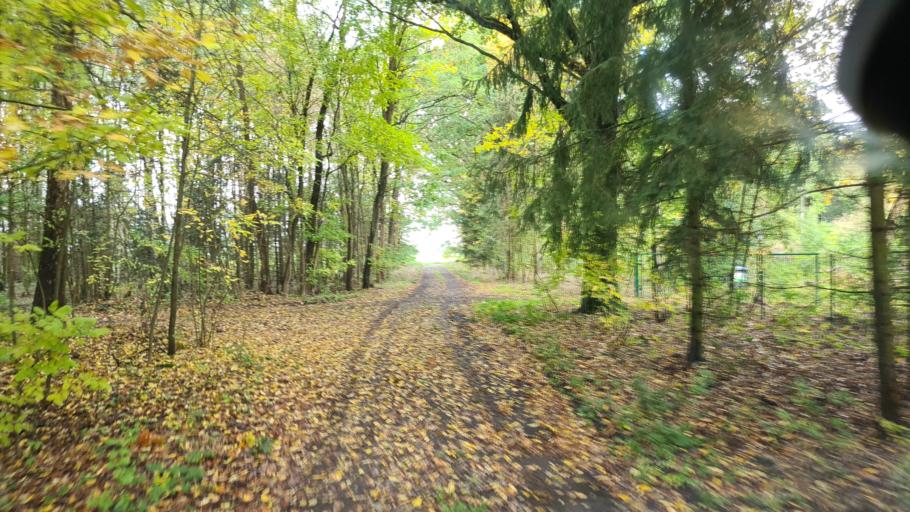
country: DE
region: Brandenburg
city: Sallgast
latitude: 51.5943
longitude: 13.8856
